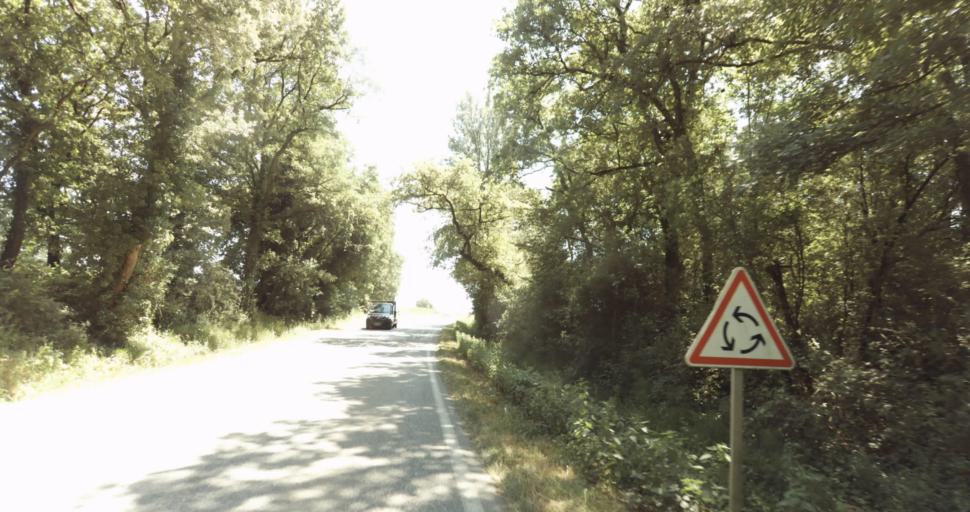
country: FR
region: Midi-Pyrenees
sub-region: Departement de la Haute-Garonne
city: La Salvetat-Saint-Gilles
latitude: 43.5933
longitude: 1.2842
